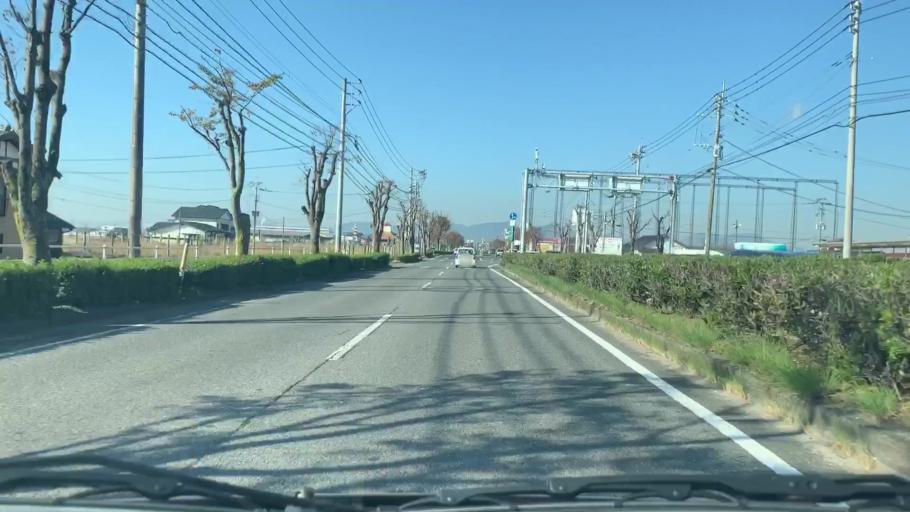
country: JP
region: Saga Prefecture
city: Saga-shi
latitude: 33.2661
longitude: 130.2525
